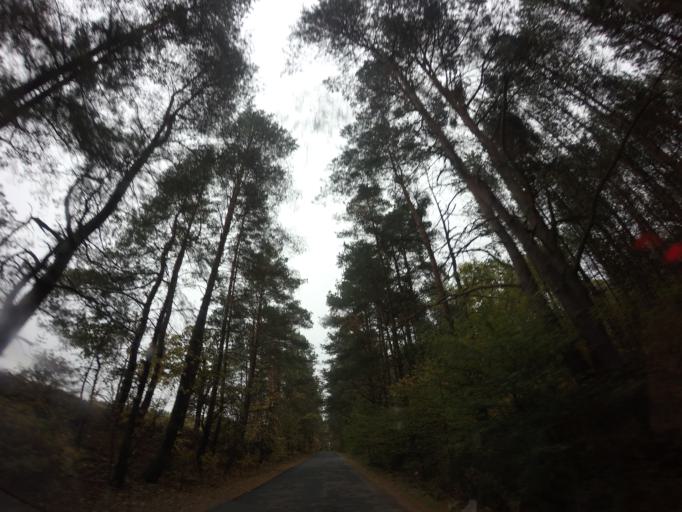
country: PL
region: West Pomeranian Voivodeship
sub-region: Powiat choszczenski
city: Bierzwnik
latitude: 53.1380
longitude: 15.6722
